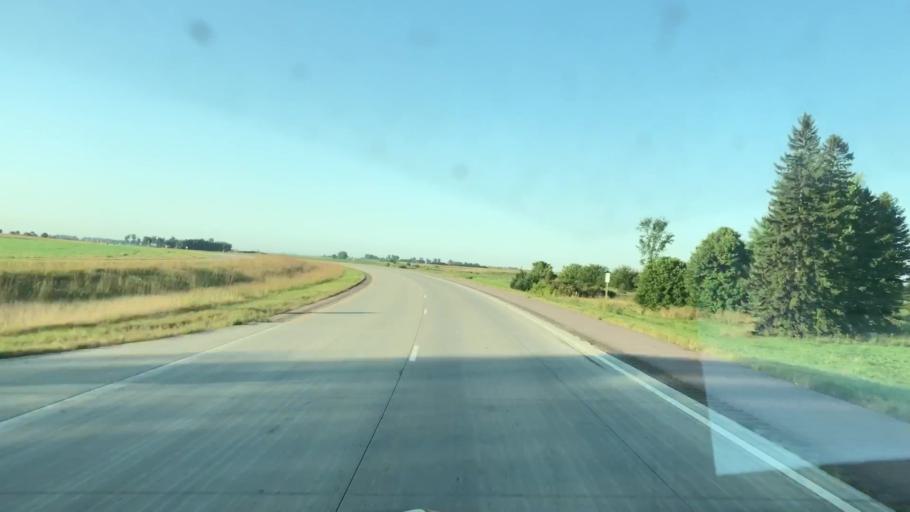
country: US
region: Minnesota
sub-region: Nobles County
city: Worthington
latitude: 43.5778
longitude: -95.6525
